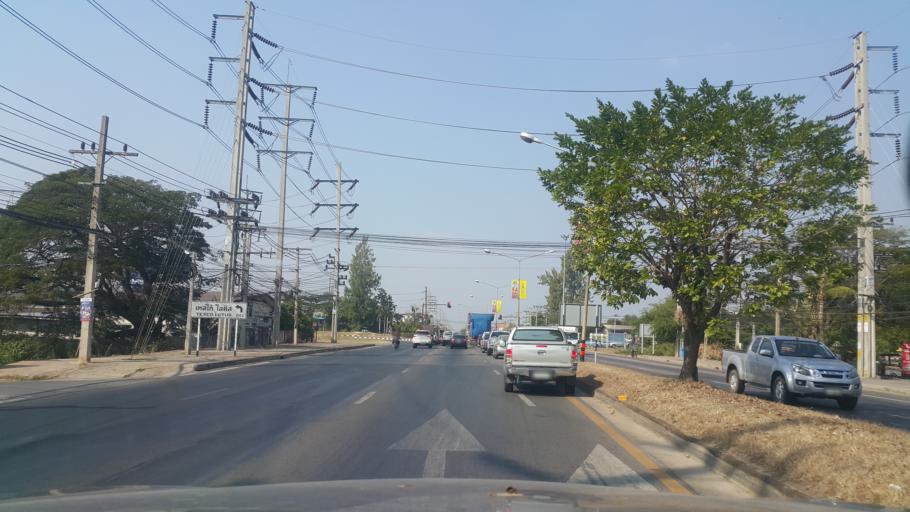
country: TH
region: Nakhon Ratchasima
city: Chok Chai
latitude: 14.7398
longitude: 102.1650
